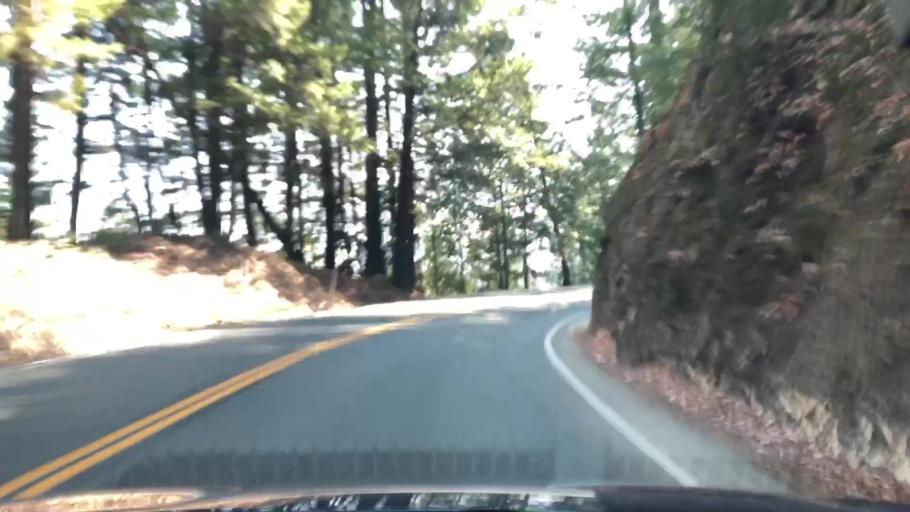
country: US
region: California
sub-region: Napa County
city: Calistoga
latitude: 38.6609
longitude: -122.5967
